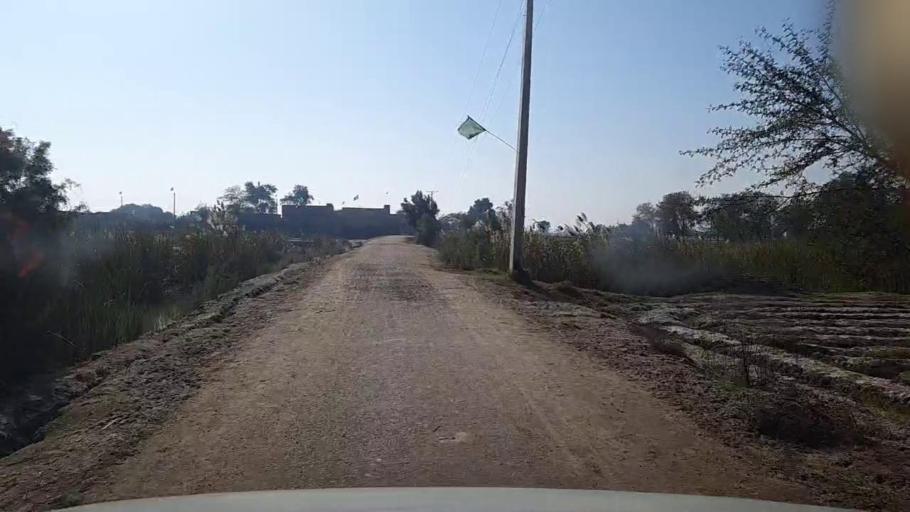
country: PK
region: Sindh
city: Khairpur
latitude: 28.0514
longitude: 69.7328
